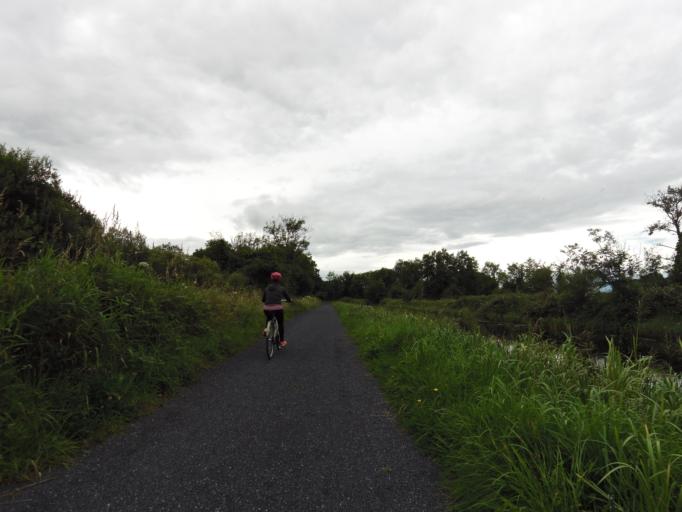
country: IE
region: Leinster
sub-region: An Iarmhi
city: An Muileann gCearr
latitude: 53.5559
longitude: -7.4808
